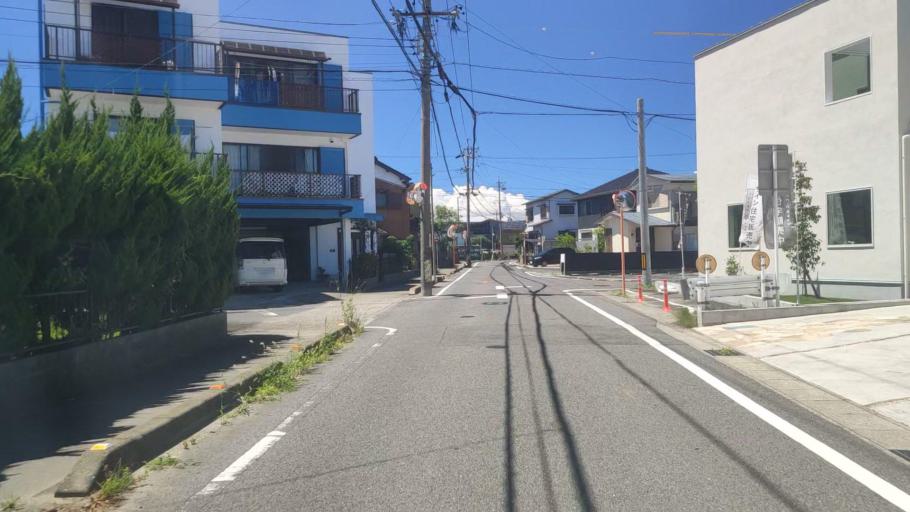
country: JP
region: Mie
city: Suzuka
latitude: 34.8534
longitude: 136.5920
